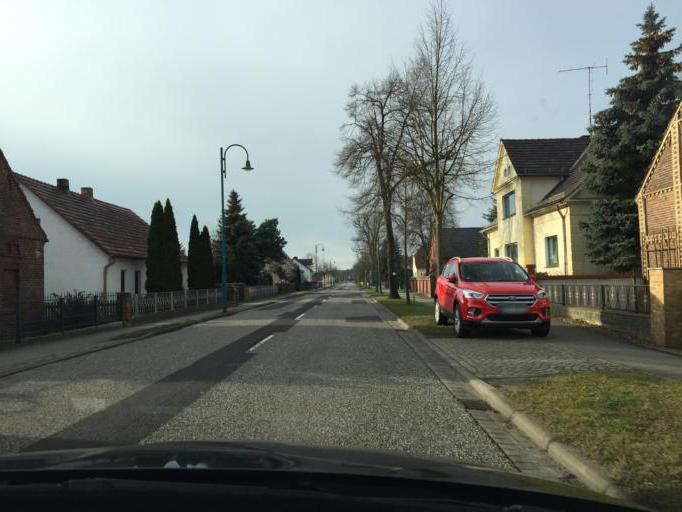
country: DE
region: Brandenburg
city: Tauer
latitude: 51.8940
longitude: 14.4467
